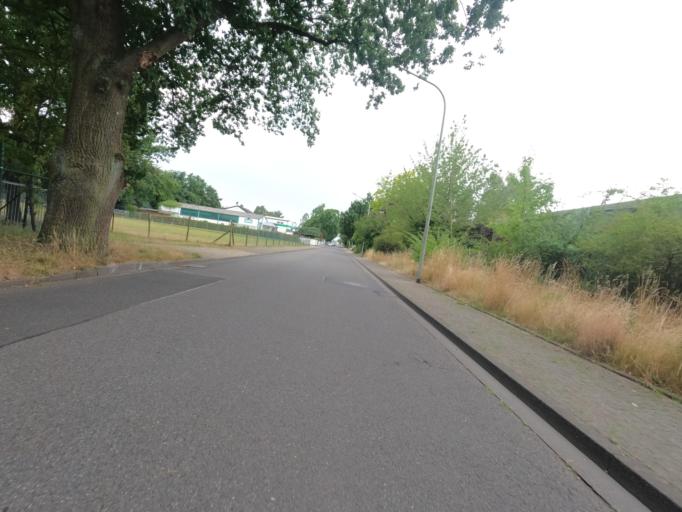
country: DE
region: North Rhine-Westphalia
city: Geilenkirchen
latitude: 50.9803
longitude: 6.1041
